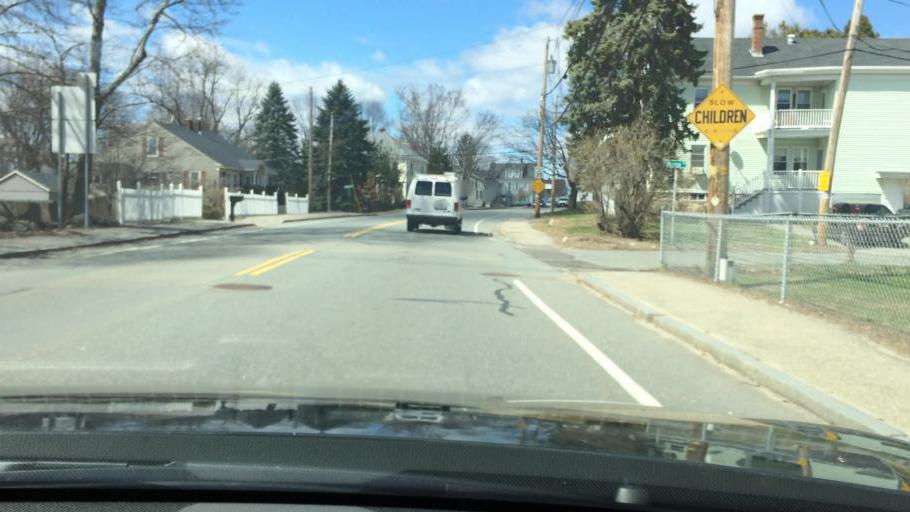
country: US
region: Massachusetts
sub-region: Essex County
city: Methuen
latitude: 42.7446
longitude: -71.1716
